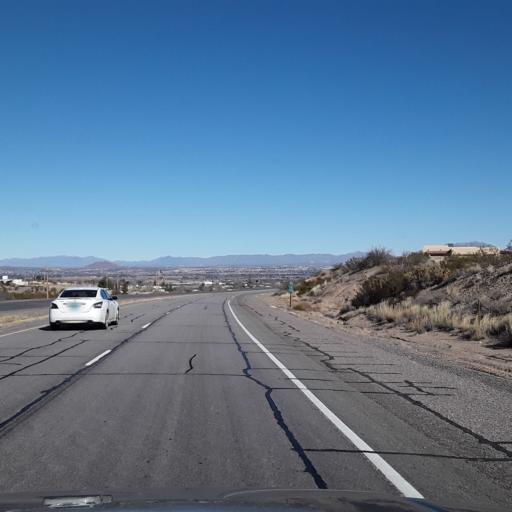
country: US
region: New Mexico
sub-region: Dona Ana County
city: Mesilla
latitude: 32.2884
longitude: -106.8737
